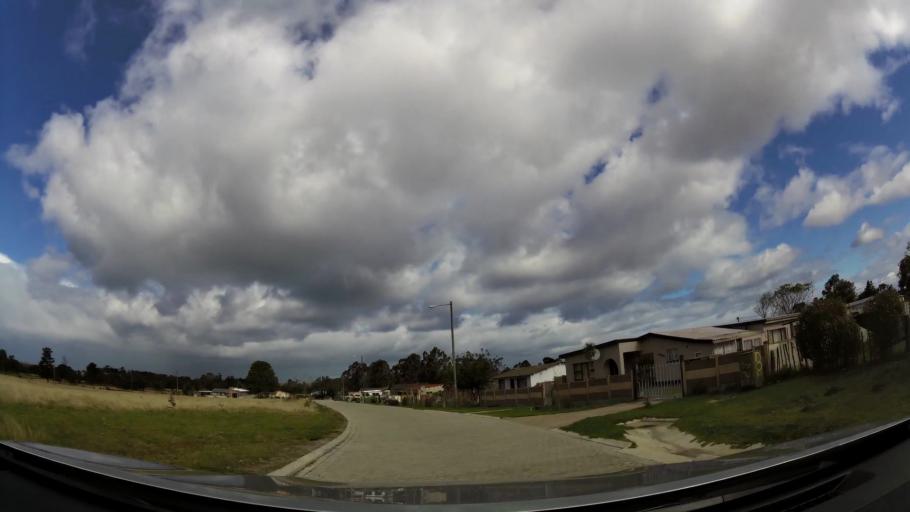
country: ZA
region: Western Cape
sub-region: Eden District Municipality
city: George
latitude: -34.0256
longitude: 22.4671
